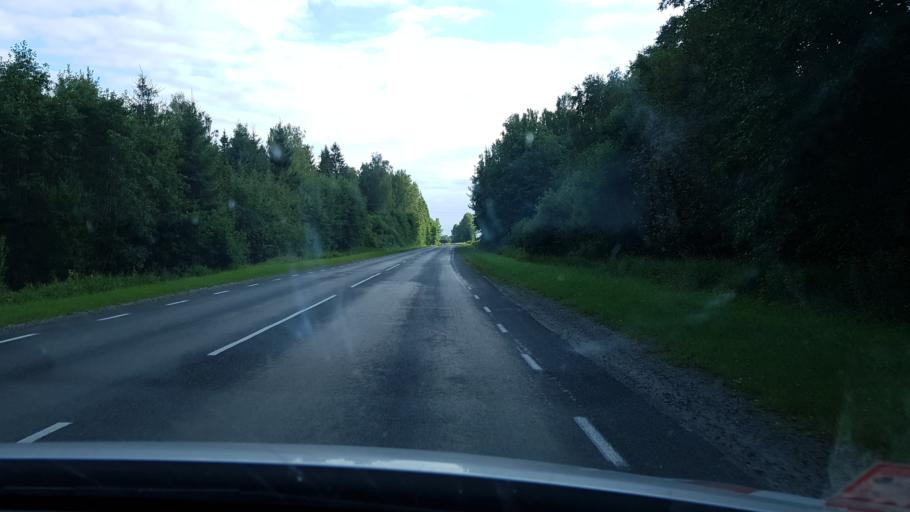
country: EE
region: Tartu
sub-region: Elva linn
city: Elva
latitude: 57.9977
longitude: 26.2675
